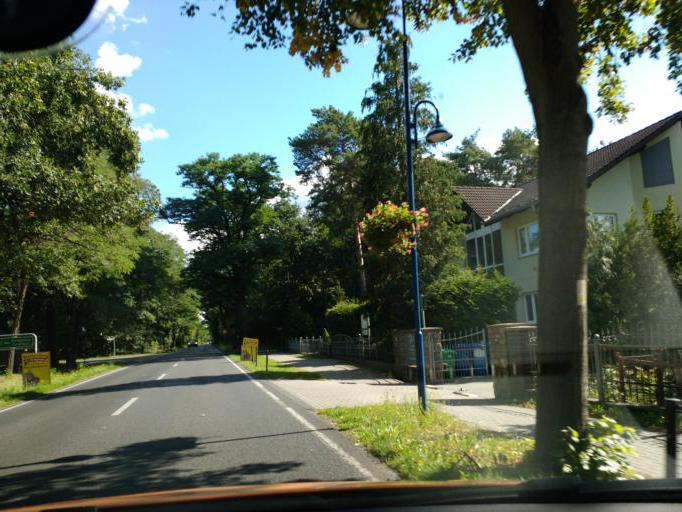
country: DE
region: Brandenburg
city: Bestensee
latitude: 52.2415
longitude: 13.6473
